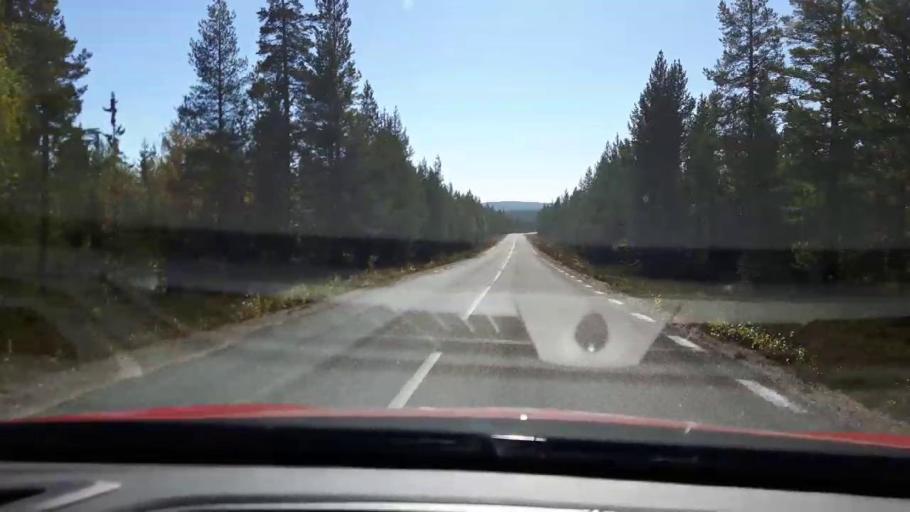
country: SE
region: Jaemtland
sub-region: Harjedalens Kommun
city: Sveg
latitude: 61.7236
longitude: 14.1670
